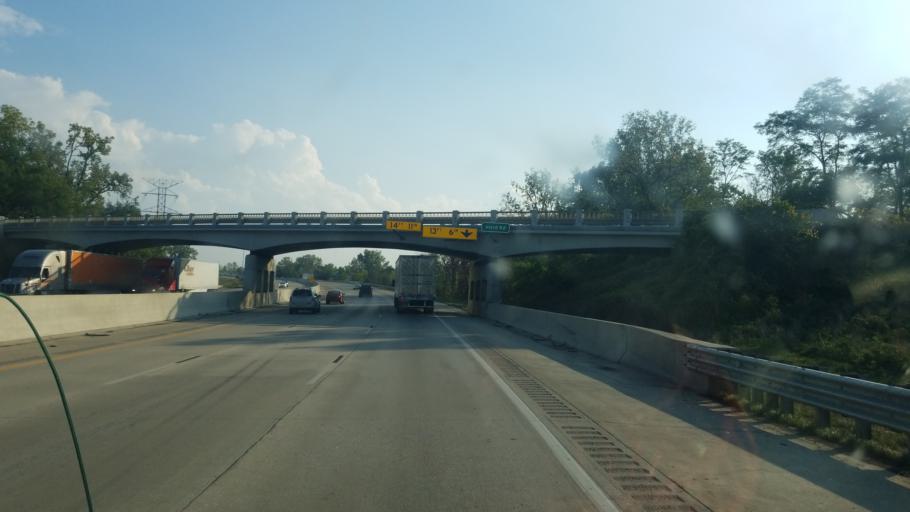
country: US
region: Michigan
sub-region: Monroe County
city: Detroit Beach
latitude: 41.9472
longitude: -83.3634
